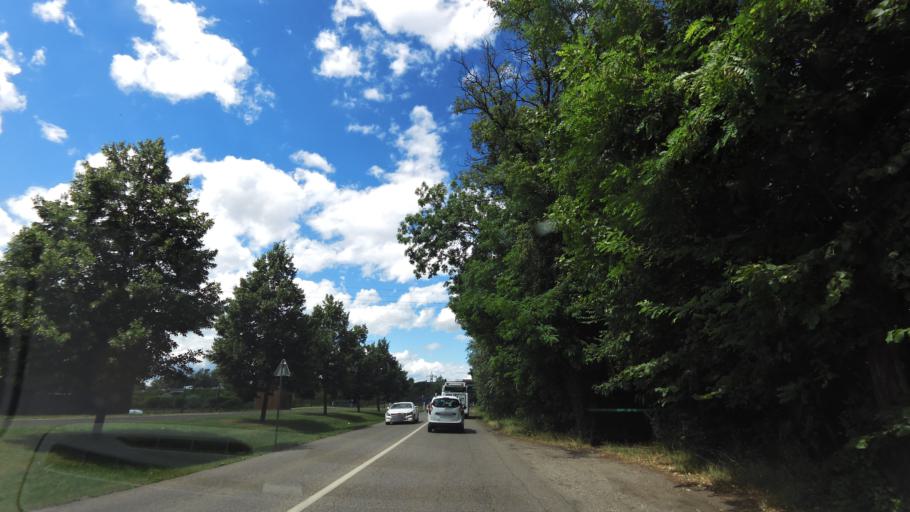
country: FR
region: Alsace
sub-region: Departement du Bas-Rhin
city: Illkirch-Graffenstaden
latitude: 48.5261
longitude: 7.6889
